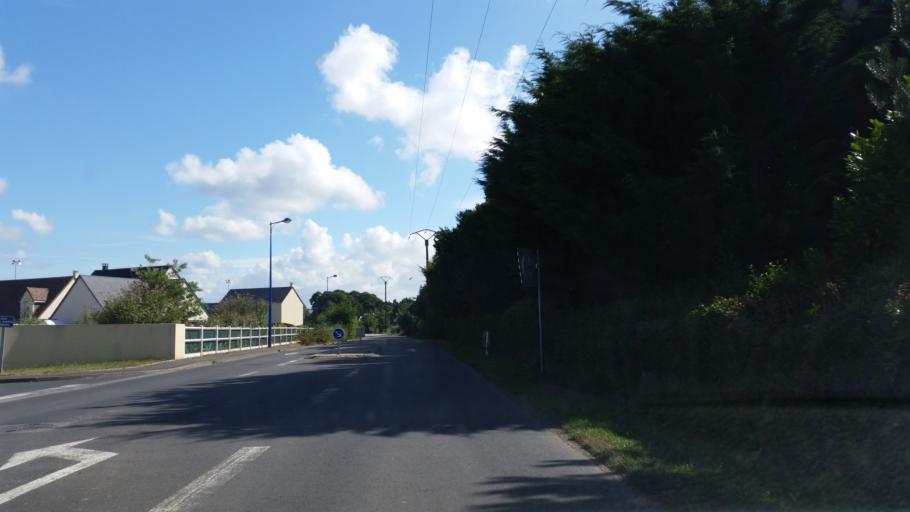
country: FR
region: Lower Normandy
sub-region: Departement du Calvados
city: Amfreville
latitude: 49.2584
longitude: -0.2314
